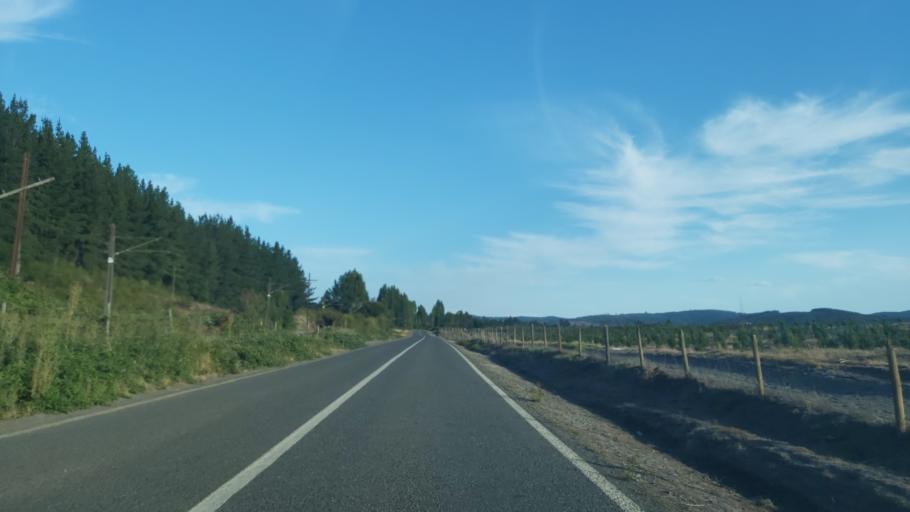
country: CL
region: Biobio
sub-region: Provincia de Concepcion
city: Lota
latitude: -37.1481
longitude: -72.9223
